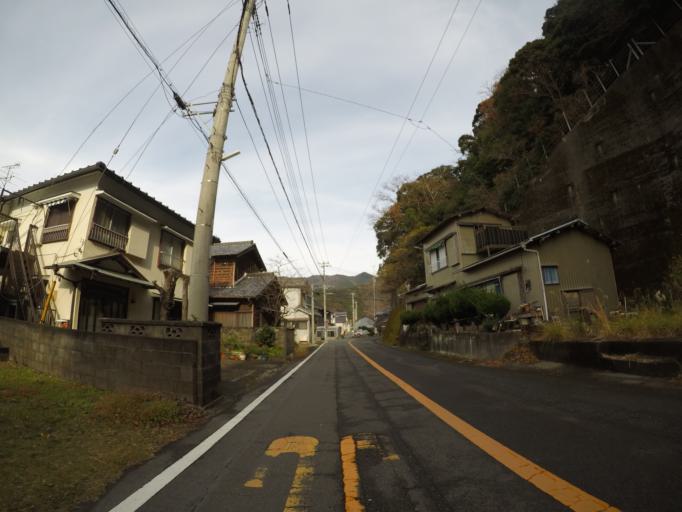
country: JP
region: Shizuoka
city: Heda
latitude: 34.8464
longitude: 138.7725
